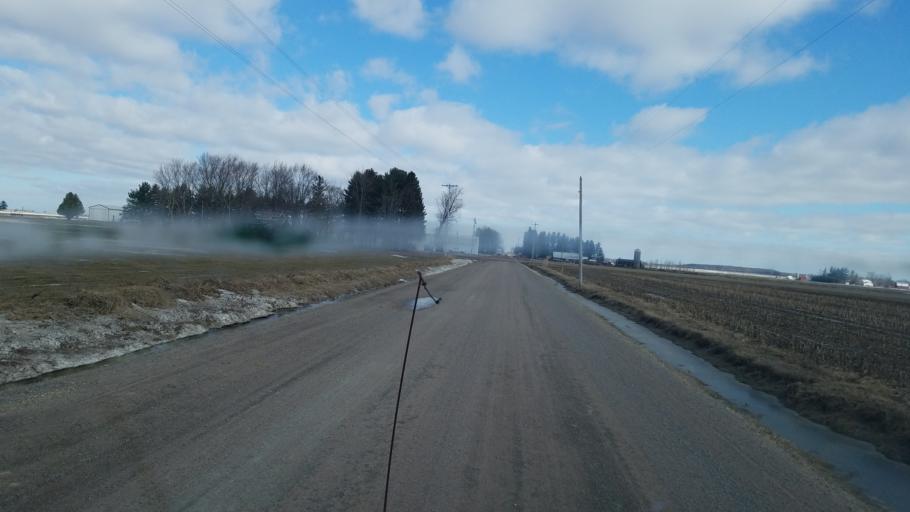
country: US
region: Wisconsin
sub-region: Clark County
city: Loyal
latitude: 44.6525
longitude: -90.4357
